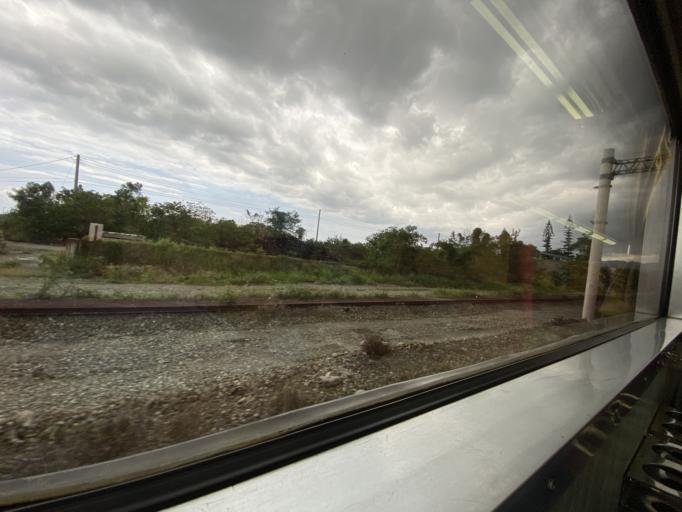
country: TW
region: Taiwan
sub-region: Taitung
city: Taitung
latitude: 22.7654
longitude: 121.0946
